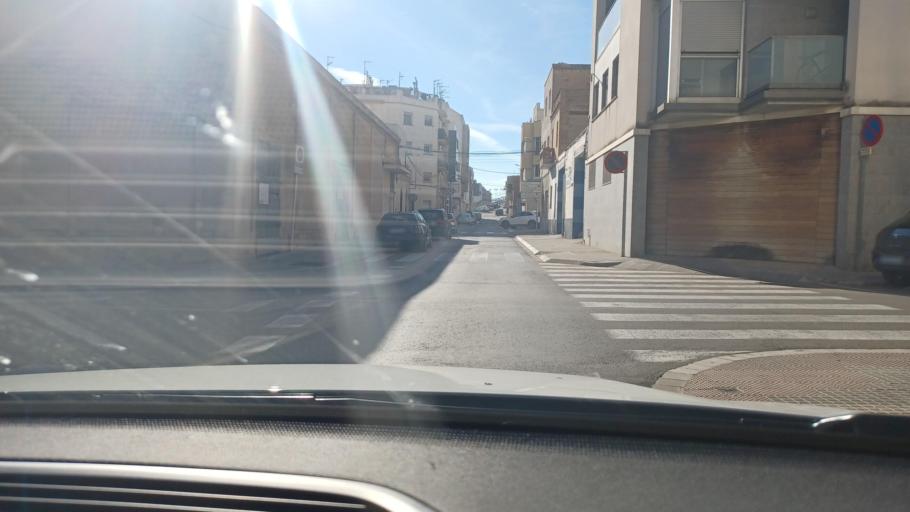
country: ES
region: Catalonia
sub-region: Provincia de Tarragona
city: Amposta
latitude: 40.7116
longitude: 0.5769
